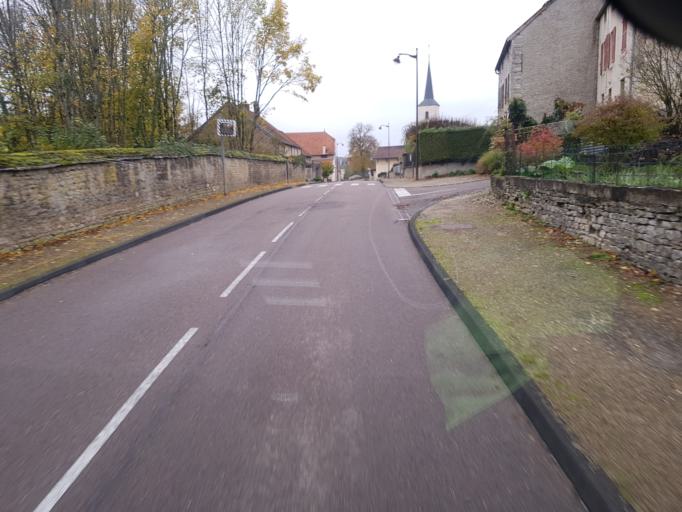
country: FR
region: Bourgogne
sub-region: Departement de la Cote-d'Or
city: Is-sur-Tille
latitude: 47.5406
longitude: 4.9690
